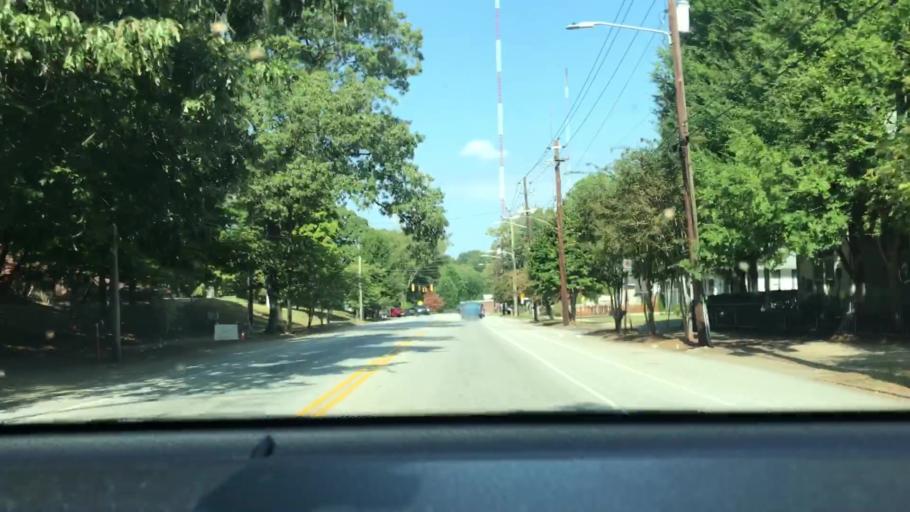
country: US
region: Georgia
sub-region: DeKalb County
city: Druid Hills
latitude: 33.7527
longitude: -84.3247
